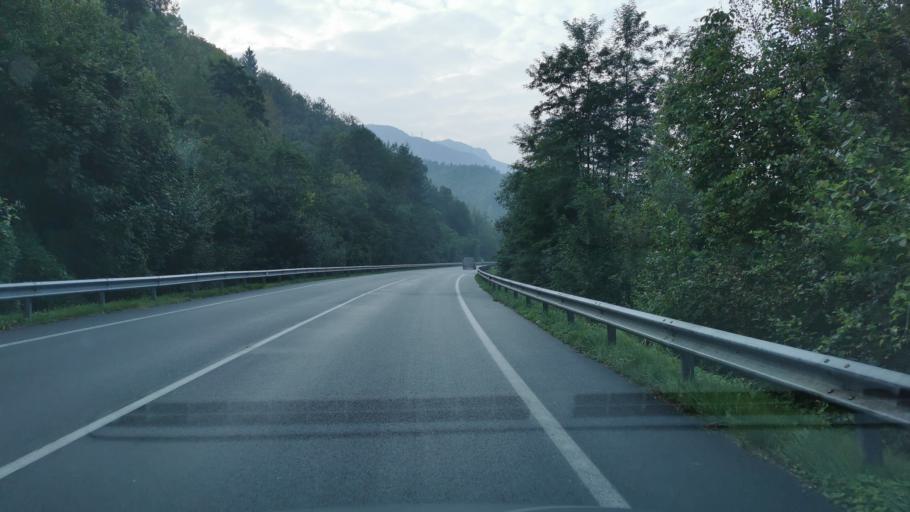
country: IT
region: Piedmont
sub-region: Provincia di Cuneo
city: Robilante
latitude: 44.3025
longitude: 7.5144
